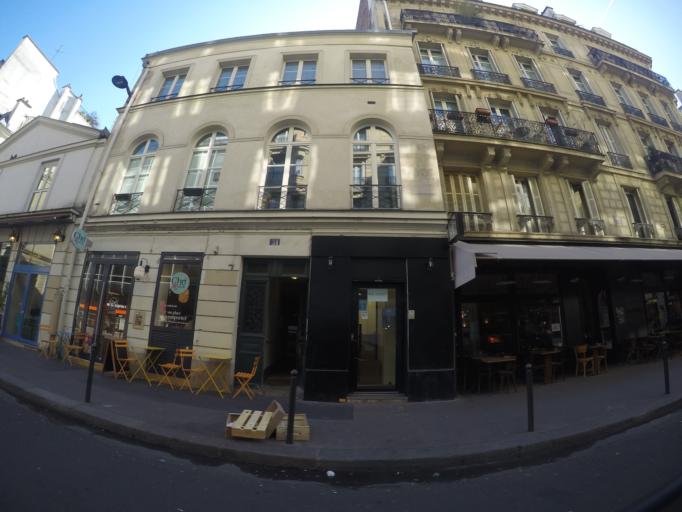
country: FR
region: Ile-de-France
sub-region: Paris
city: Paris
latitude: 48.8753
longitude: 2.3513
